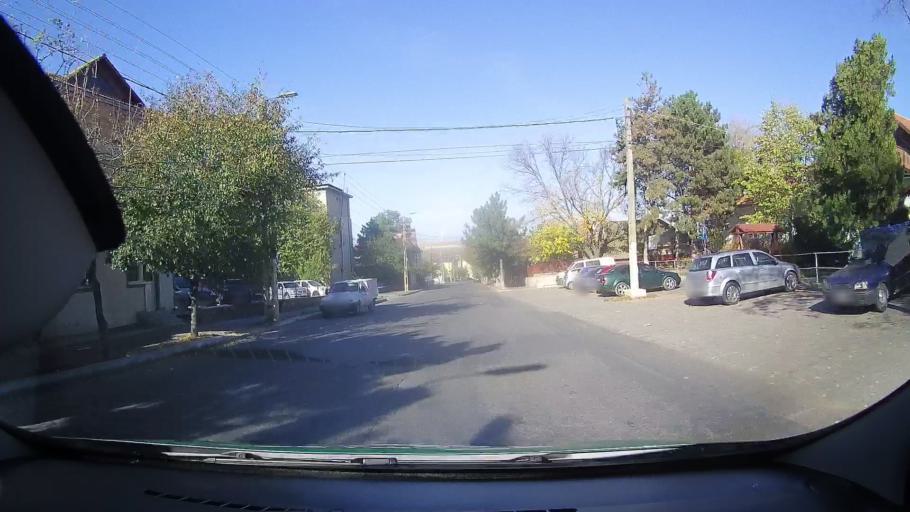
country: RO
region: Tulcea
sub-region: Oras Babadag
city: Babadag
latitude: 44.8906
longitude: 28.7277
